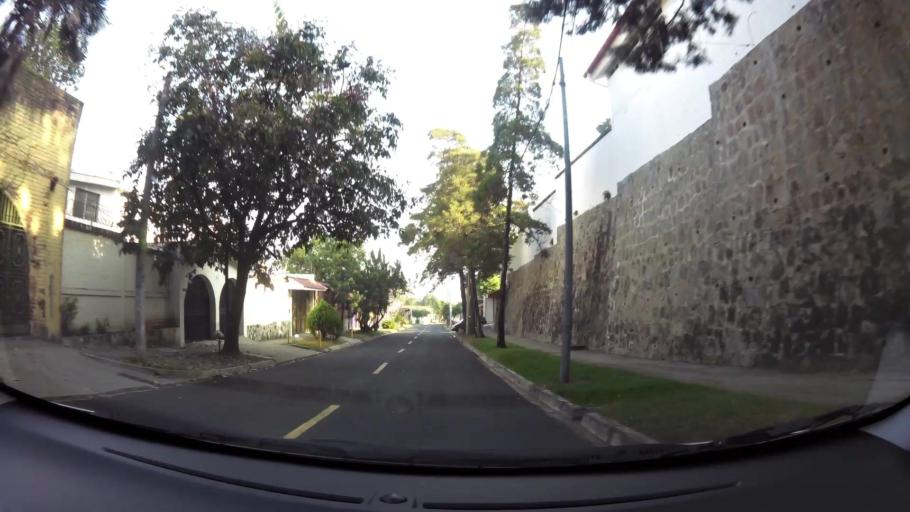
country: SV
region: La Libertad
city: Antiguo Cuscatlan
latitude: 13.6778
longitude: -89.2228
